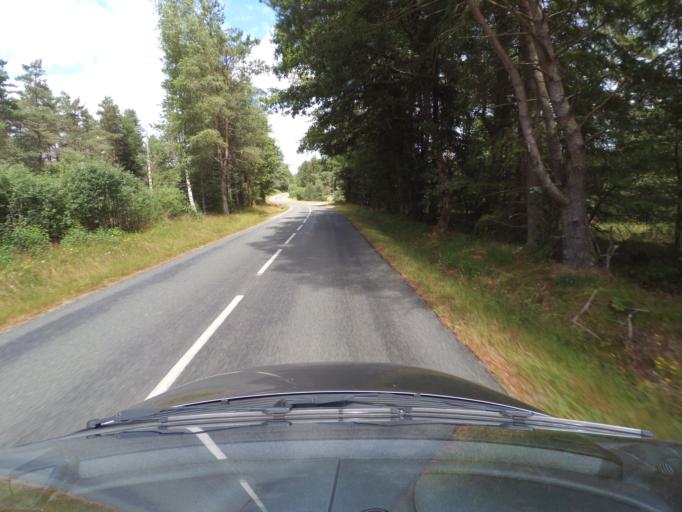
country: FR
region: Limousin
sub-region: Departement de la Haute-Vienne
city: Peyrat-le-Chateau
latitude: 45.8558
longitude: 1.9017
